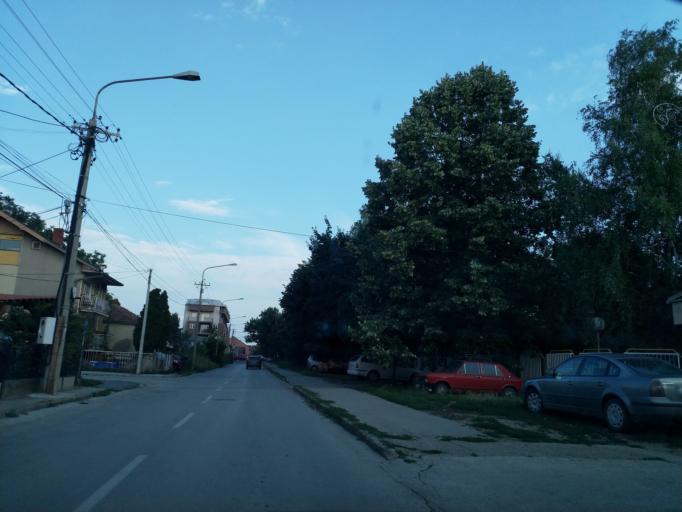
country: RS
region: Central Serbia
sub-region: Pomoravski Okrug
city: Jagodina
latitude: 43.9739
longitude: 21.2535
